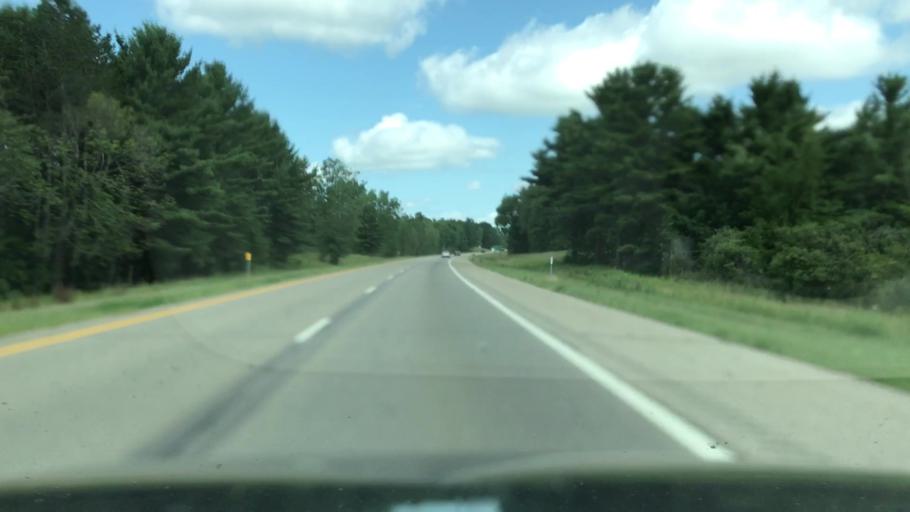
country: US
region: Michigan
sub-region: Mecosta County
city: Big Rapids
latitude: 43.6973
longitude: -85.5259
